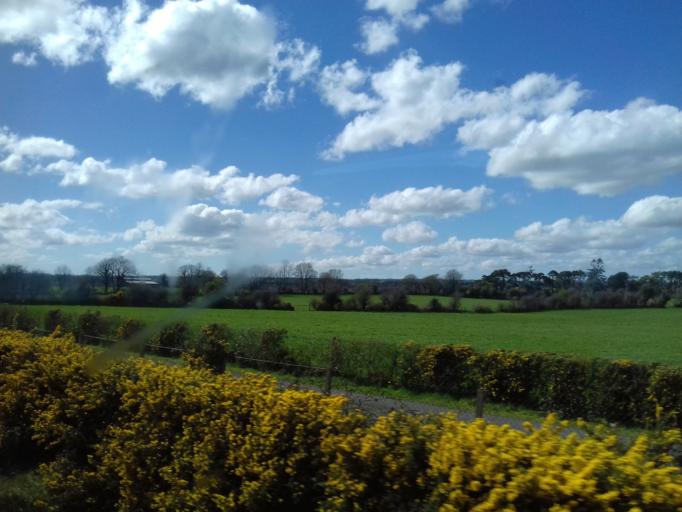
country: IE
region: Munster
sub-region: County Cork
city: Kanturk
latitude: 52.1032
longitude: -8.9519
